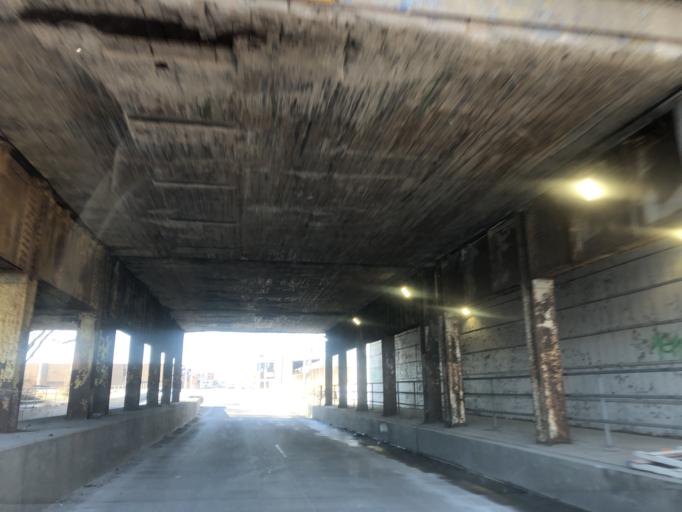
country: US
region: Illinois
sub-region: Cook County
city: Evergreen Park
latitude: 41.7502
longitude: -87.6779
